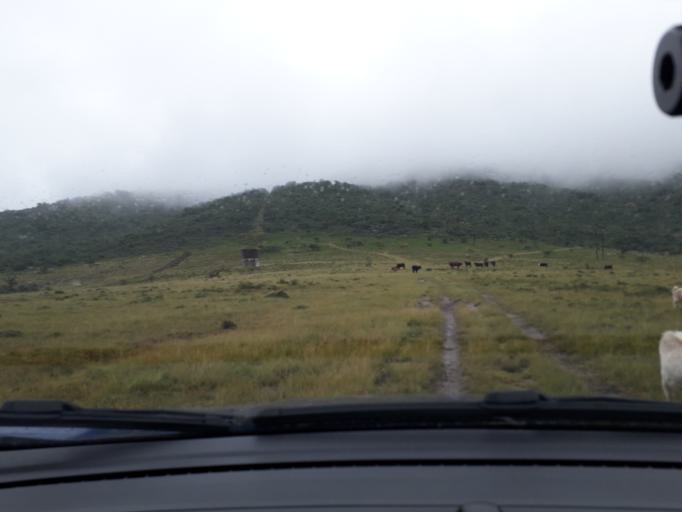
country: ZA
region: Eastern Cape
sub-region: Buffalo City Metropolitan Municipality
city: Bhisho
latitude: -32.7311
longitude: 27.3706
